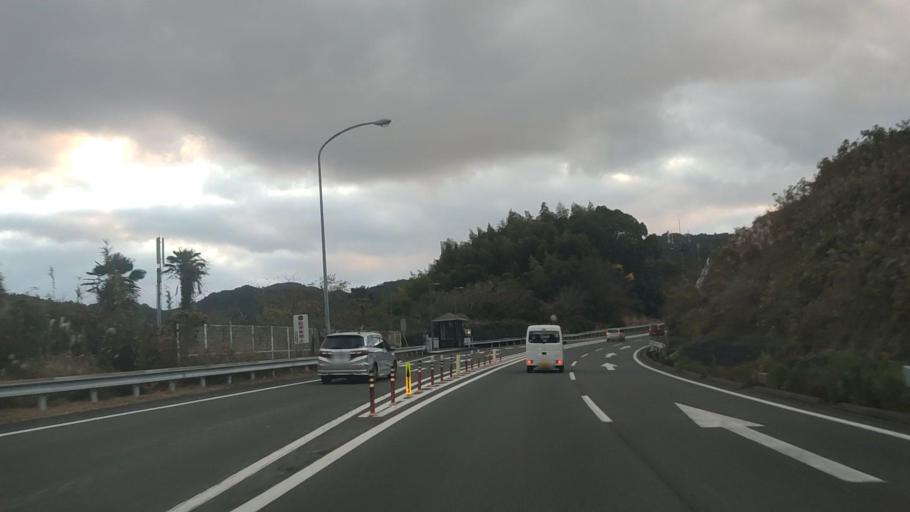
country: JP
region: Nagasaki
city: Obita
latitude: 32.8114
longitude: 129.9364
